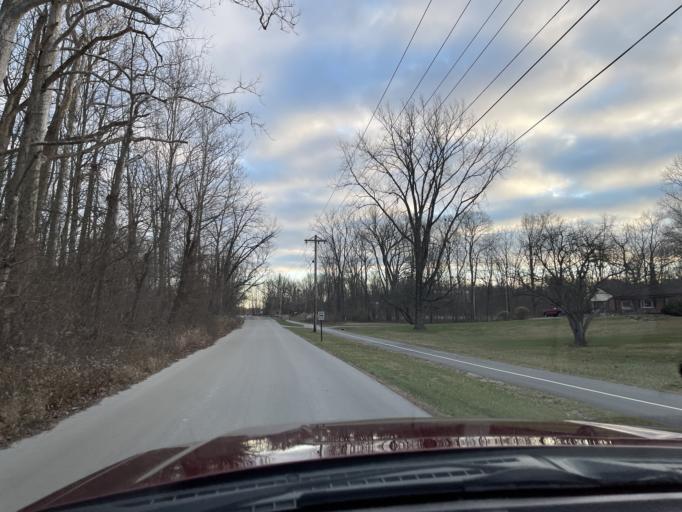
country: US
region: Indiana
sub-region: Hendricks County
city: Avon
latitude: 39.7763
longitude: -86.4214
